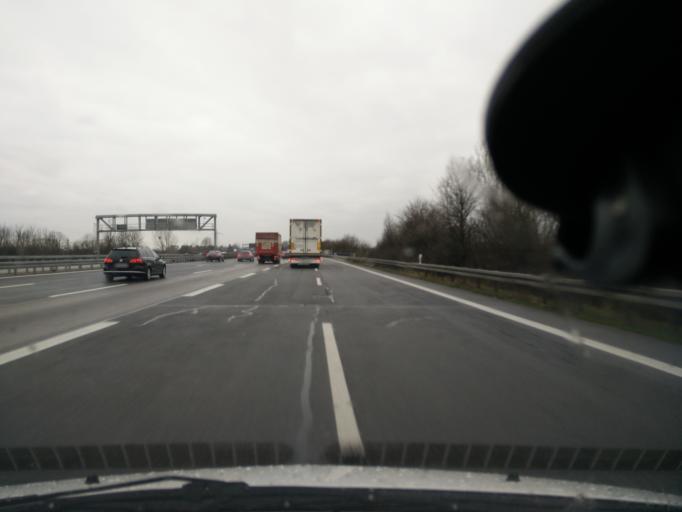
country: DE
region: Bavaria
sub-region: Upper Bavaria
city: Oberschleissheim
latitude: 48.2257
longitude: 11.5360
